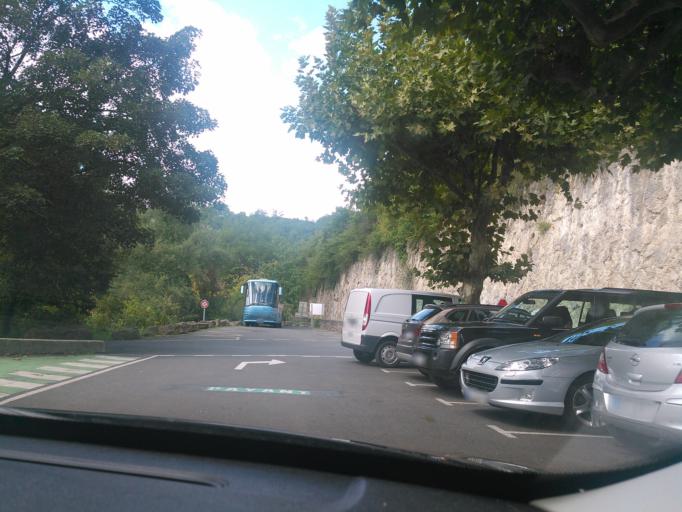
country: FR
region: Aquitaine
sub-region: Departement de la Dordogne
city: Cenac-et-Saint-Julien
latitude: 44.8401
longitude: 1.1406
